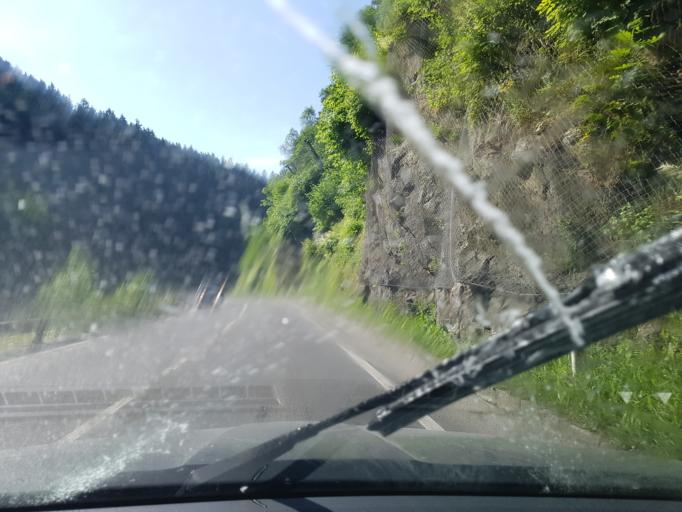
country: AT
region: Carinthia
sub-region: Politischer Bezirk Spittal an der Drau
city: Spittal an der Drau
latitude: 46.8094
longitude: 13.4947
